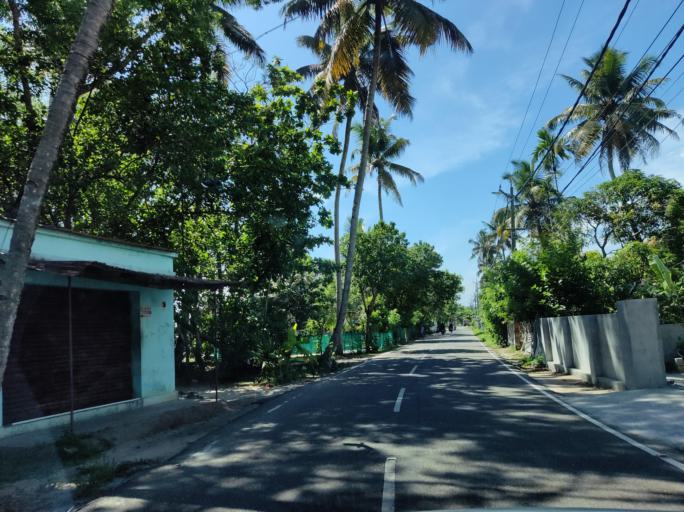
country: IN
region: Kerala
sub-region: Alappuzha
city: Kayankulam
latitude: 9.1813
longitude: 76.4431
